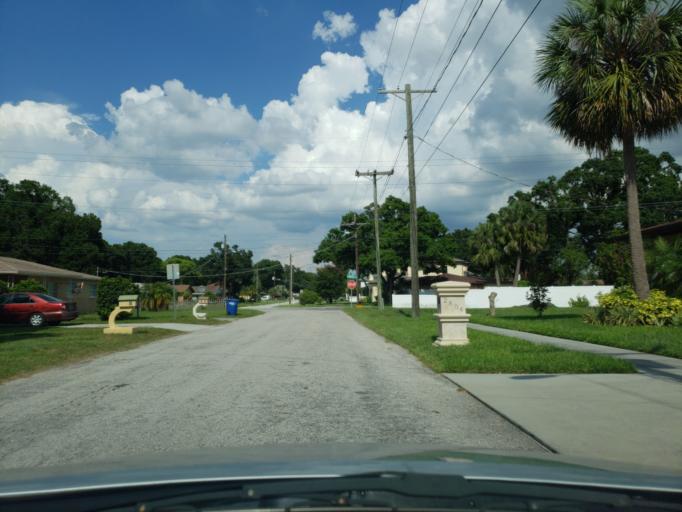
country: US
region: Florida
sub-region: Hillsborough County
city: Tampa
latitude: 27.9762
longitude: -82.4895
